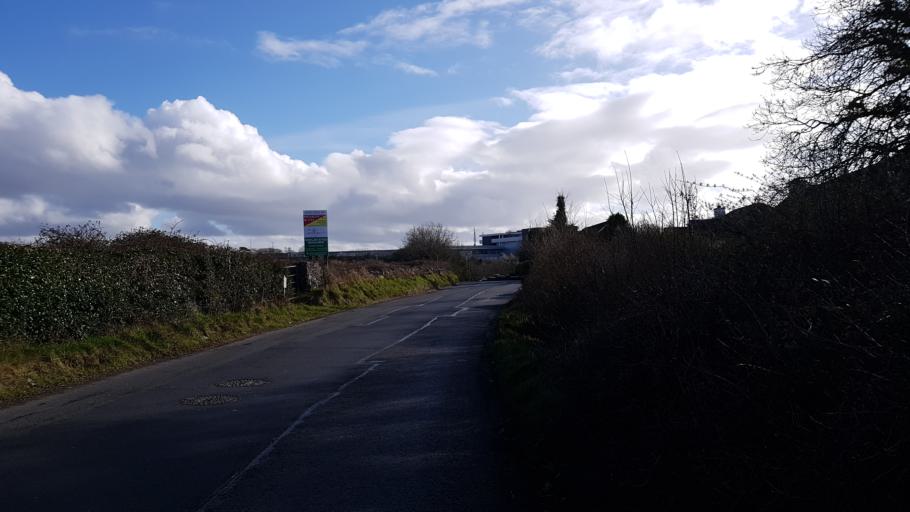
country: IE
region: Connaught
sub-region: County Galway
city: Gaillimh
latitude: 53.2982
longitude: -9.0170
